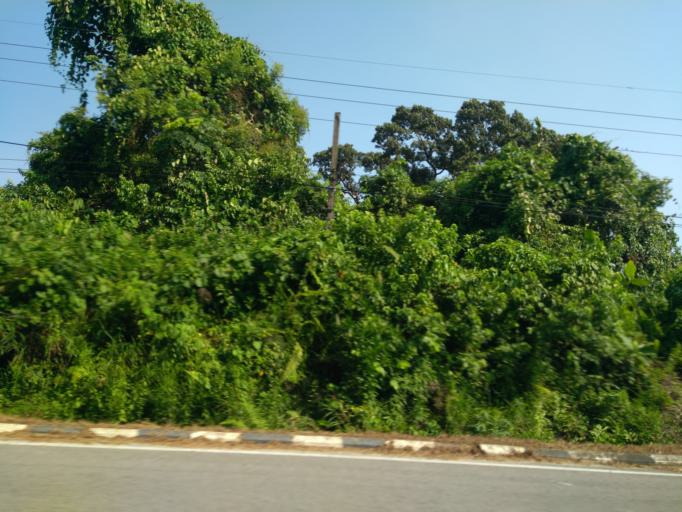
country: MY
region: Sarawak
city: Kuching
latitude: 1.7191
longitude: 110.3256
